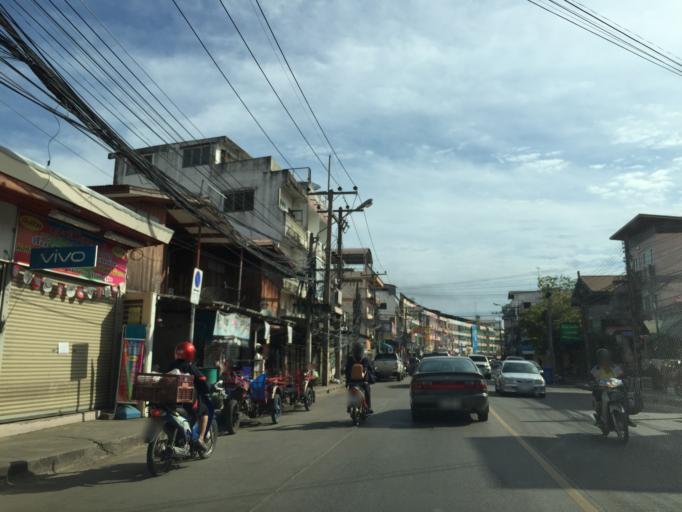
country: TH
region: Phitsanulok
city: Phitsanulok
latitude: 16.8203
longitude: 100.2667
